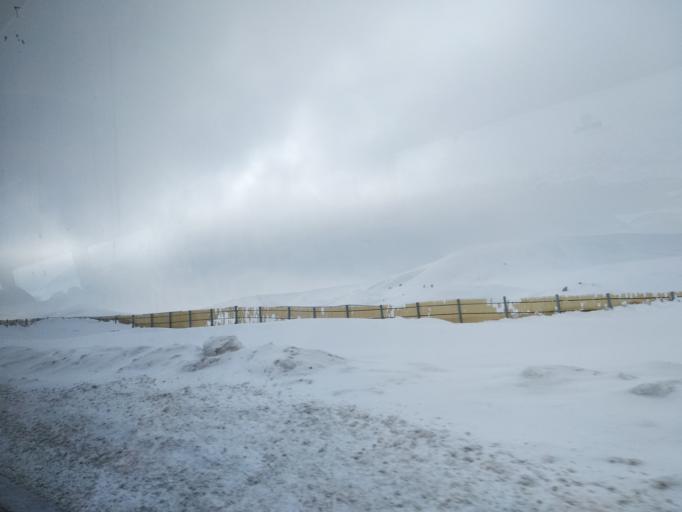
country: TR
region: Erzincan
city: Catalarmut
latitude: 39.8924
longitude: 39.3680
